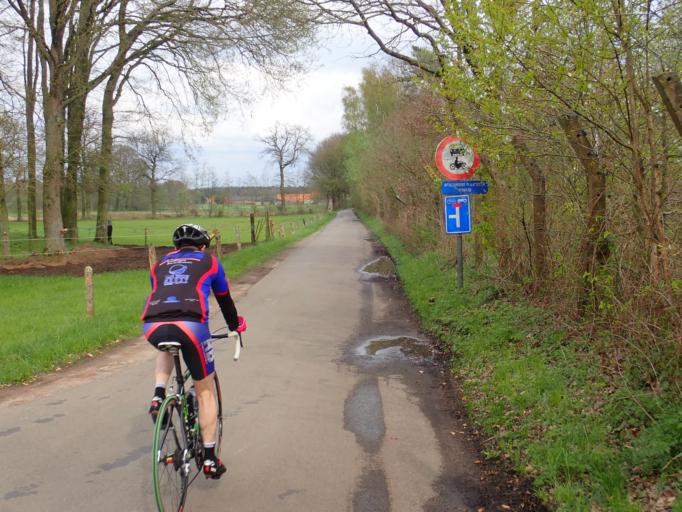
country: BE
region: Flanders
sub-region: Provincie Antwerpen
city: Vorselaar
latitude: 51.1860
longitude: 4.7680
